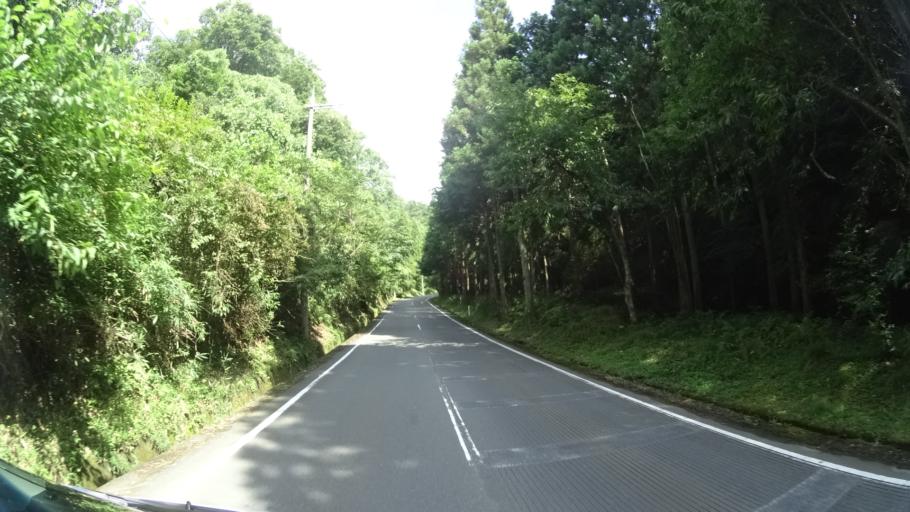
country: JP
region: Kyoto
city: Fukuchiyama
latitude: 35.3465
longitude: 135.1545
